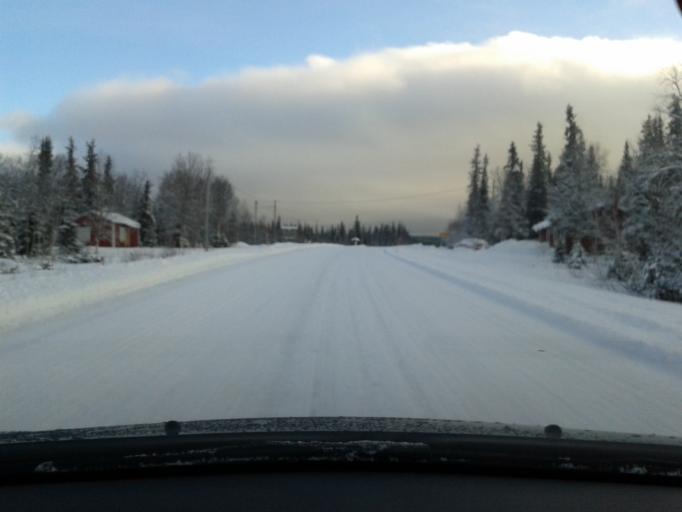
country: SE
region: Vaesterbotten
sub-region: Vilhelmina Kommun
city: Sjoberg
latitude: 65.2575
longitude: 15.6918
